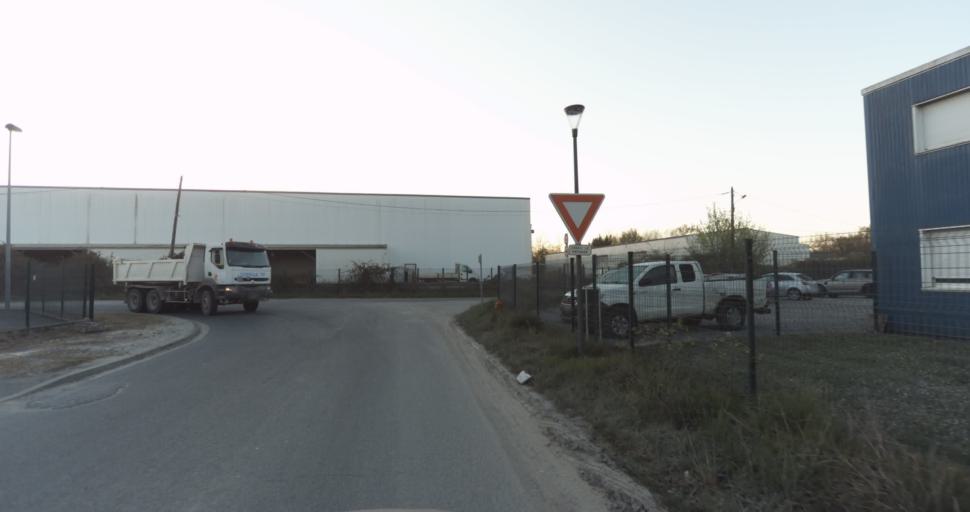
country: FR
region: Aquitaine
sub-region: Departement de la Gironde
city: Saint-Aubin-de-Medoc
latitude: 44.8123
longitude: -0.7267
